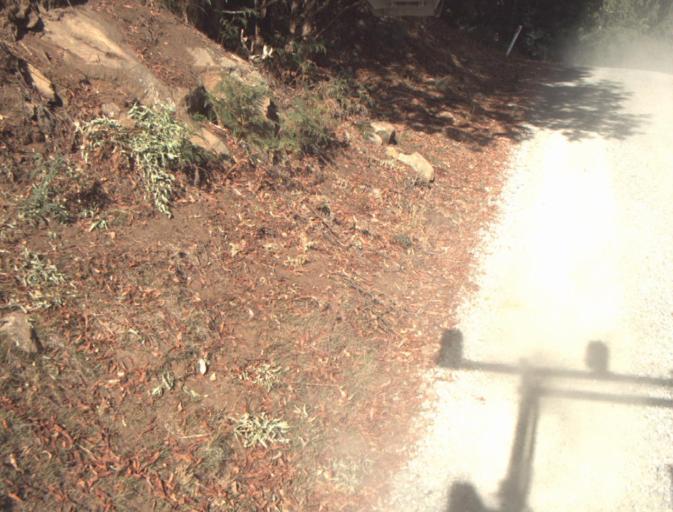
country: AU
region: Tasmania
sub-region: Launceston
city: Mayfield
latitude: -41.2875
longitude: 147.1941
